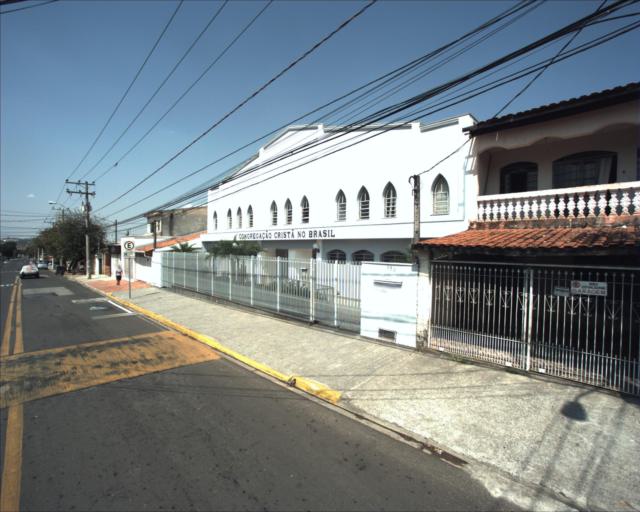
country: BR
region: Sao Paulo
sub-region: Sorocaba
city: Sorocaba
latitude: -23.4330
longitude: -47.4614
